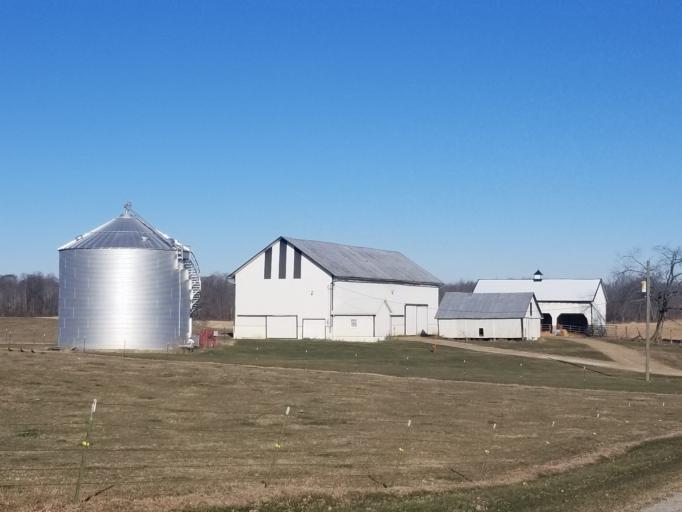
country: US
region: Ohio
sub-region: Knox County
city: Centerburg
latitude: 40.4086
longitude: -82.6810
